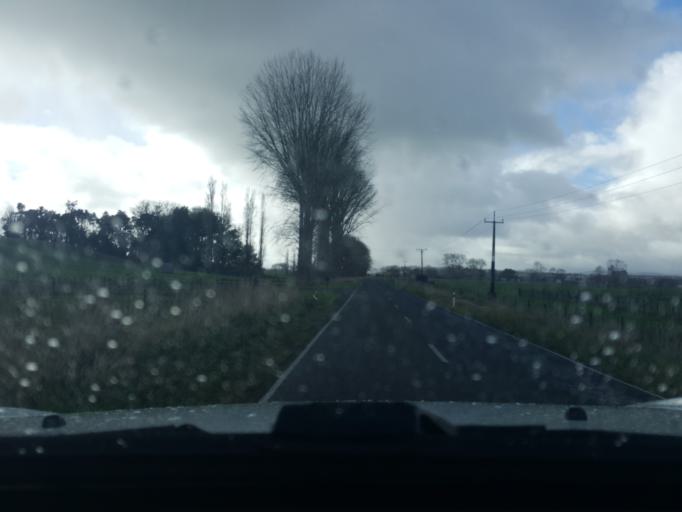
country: NZ
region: Waikato
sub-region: Waikato District
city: Te Kauwhata
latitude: -37.4478
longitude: 175.1071
